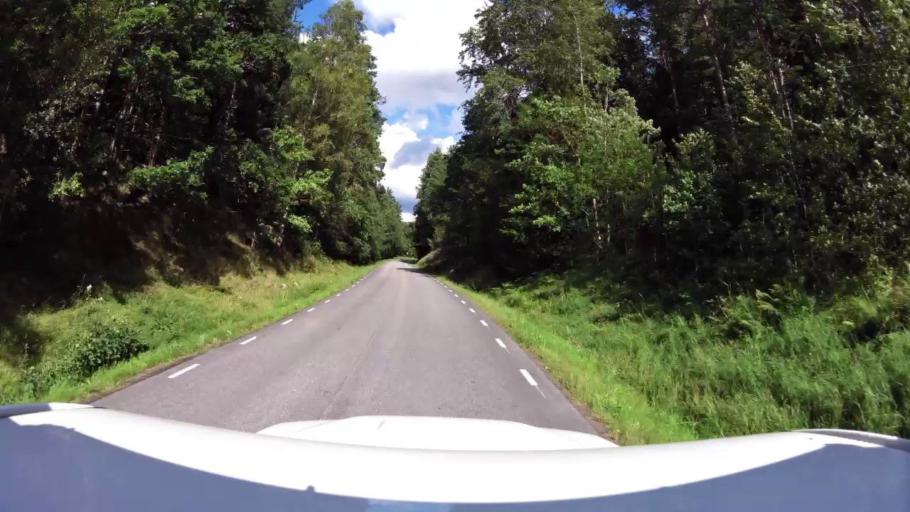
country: SE
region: OEstergoetland
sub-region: Kinda Kommun
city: Rimforsa
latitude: 58.2261
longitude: 15.7120
